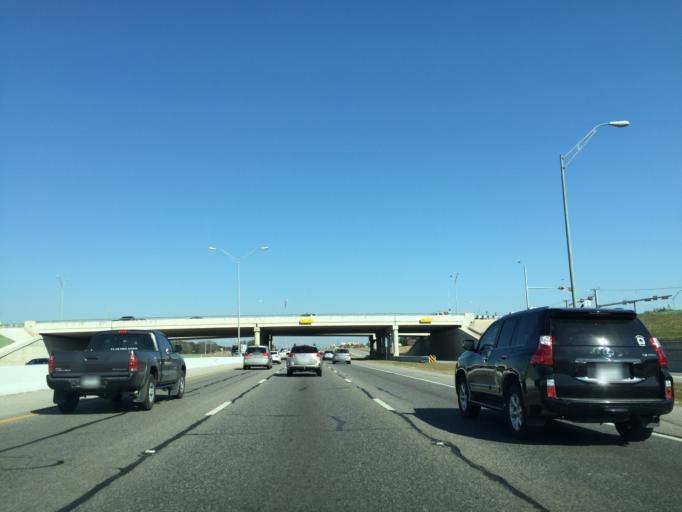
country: US
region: Texas
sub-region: Williamson County
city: Round Rock
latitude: 30.5569
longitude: -97.6924
